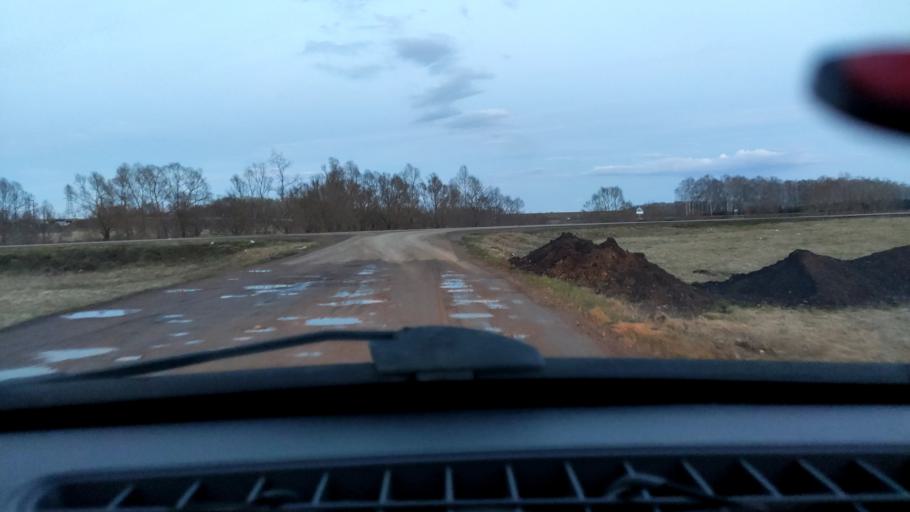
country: RU
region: Bashkortostan
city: Ulukulevo
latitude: 54.4195
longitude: 56.3423
